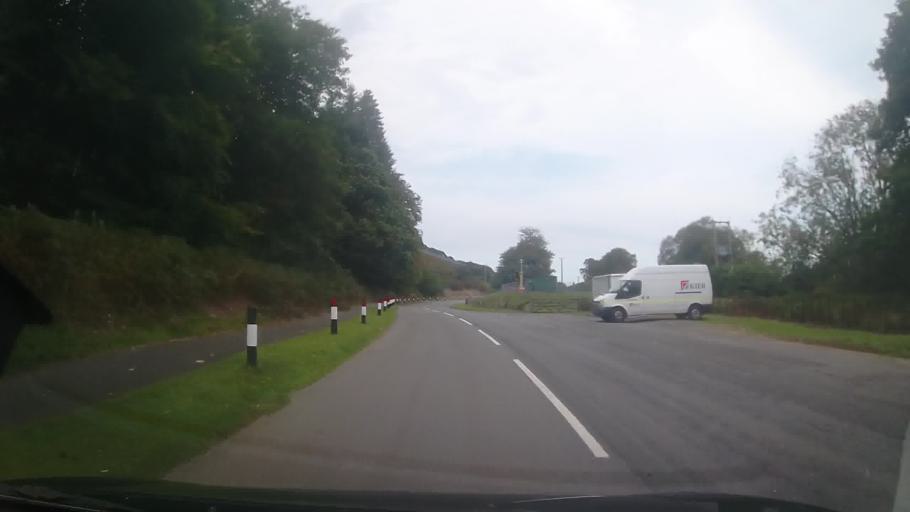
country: GB
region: Wales
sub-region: Sir Powys
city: Rhayader
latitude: 52.2732
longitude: -3.5673
